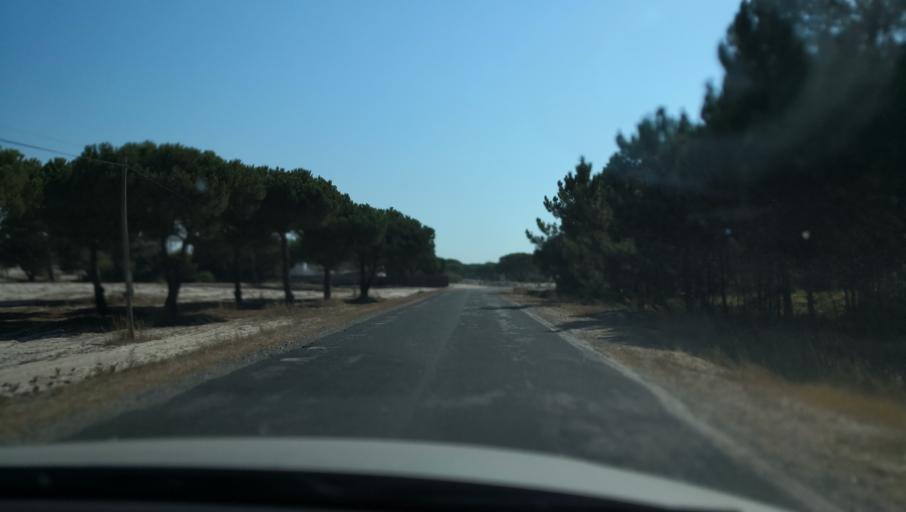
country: PT
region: Setubal
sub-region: Setubal
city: Setubal
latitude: 38.4039
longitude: -8.7546
